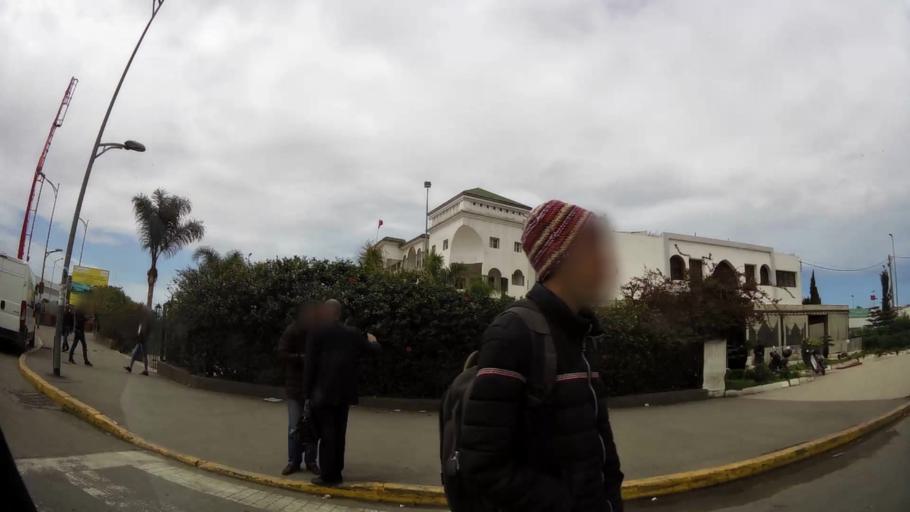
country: MA
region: Grand Casablanca
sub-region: Mediouna
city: Tit Mellil
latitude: 33.6103
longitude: -7.5068
